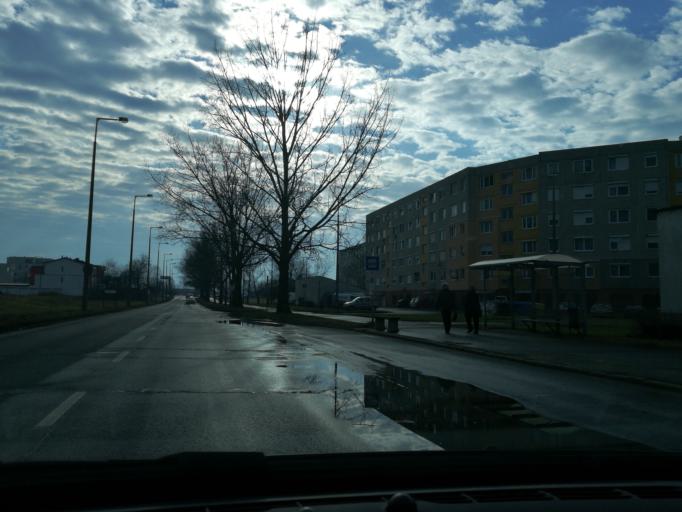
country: HU
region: Szabolcs-Szatmar-Bereg
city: Nyiregyhaza
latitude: 47.9580
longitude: 21.7439
